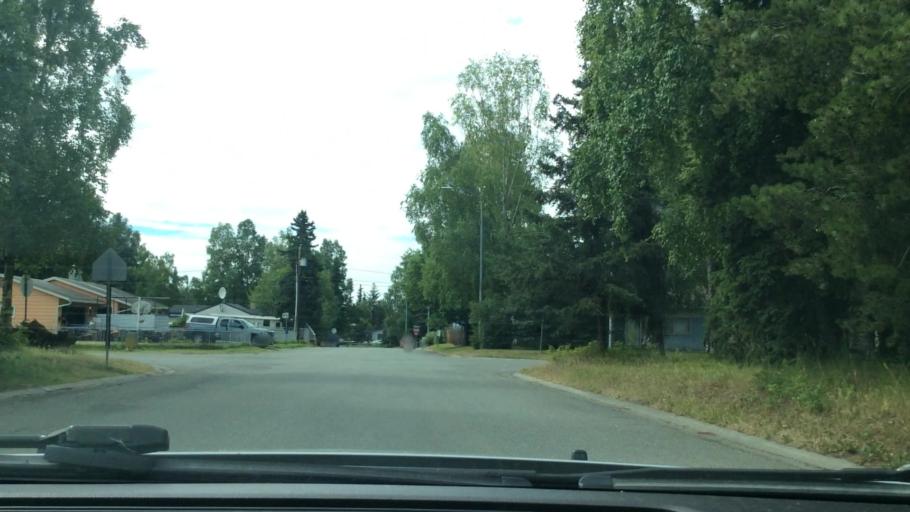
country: US
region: Alaska
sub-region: Anchorage Municipality
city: Anchorage
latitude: 61.2202
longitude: -149.7872
